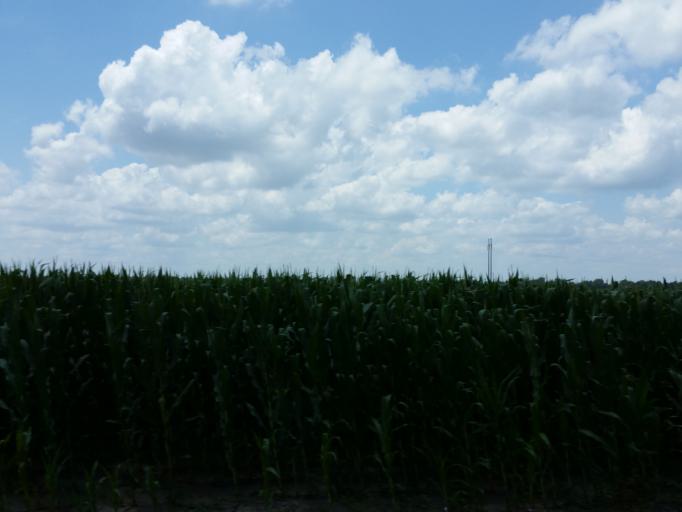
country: US
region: Tennessee
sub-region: Lake County
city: Ridgely
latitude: 36.2099
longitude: -89.4636
